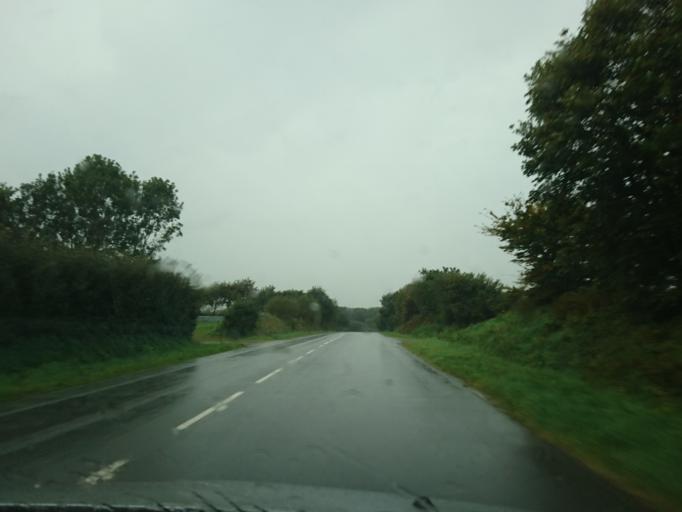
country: FR
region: Brittany
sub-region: Departement du Finistere
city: Plouvien
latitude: 48.5310
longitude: -4.4701
